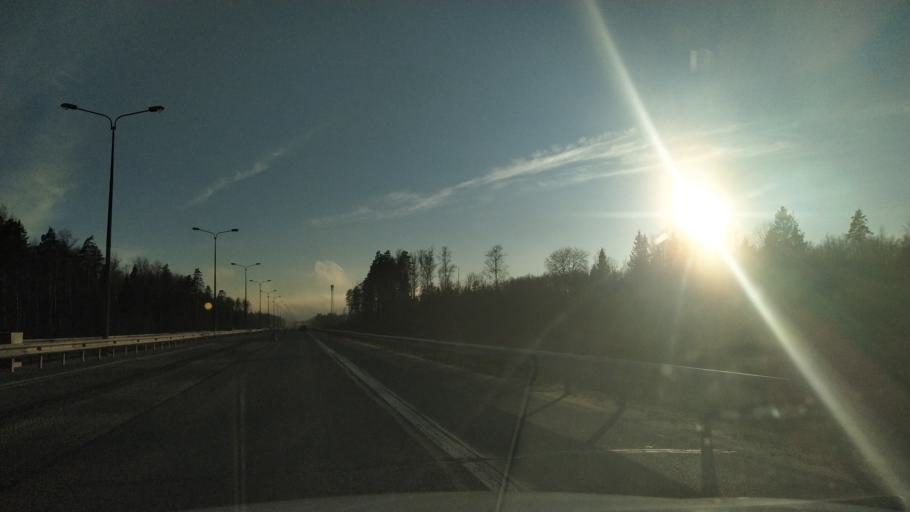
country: RU
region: St.-Petersburg
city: Ol'gino
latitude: 60.0499
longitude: 30.0766
